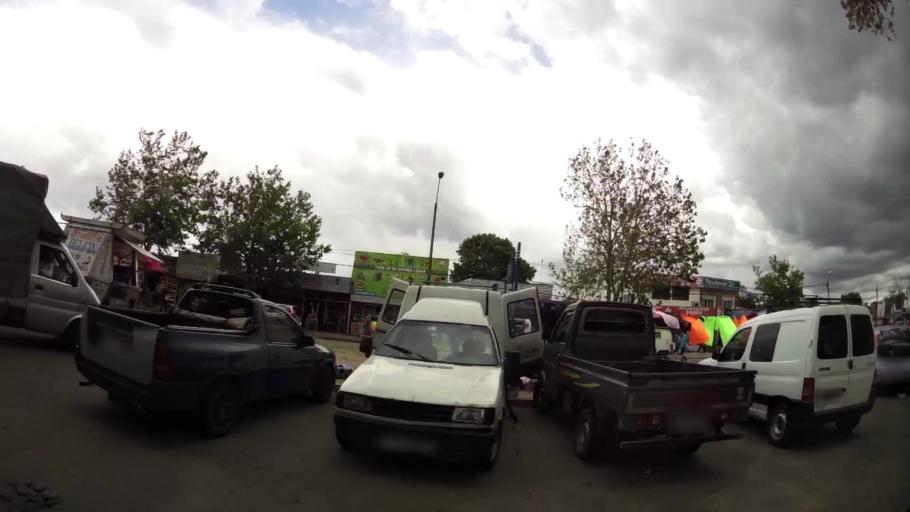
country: UY
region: Montevideo
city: Montevideo
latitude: -34.8254
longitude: -56.1408
